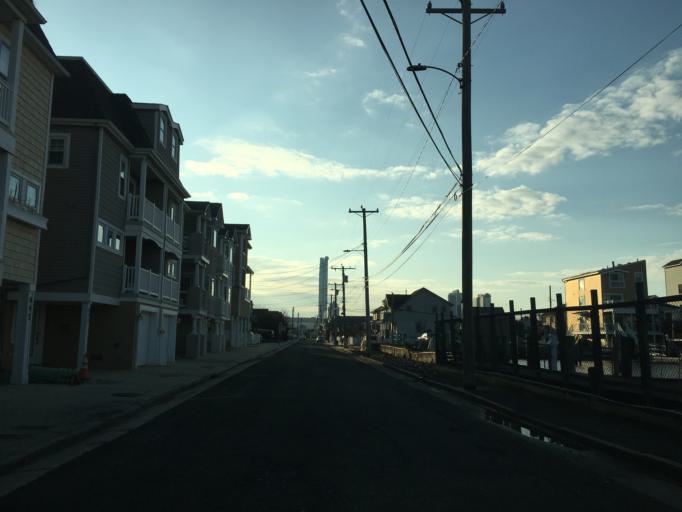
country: US
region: New Jersey
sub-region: Atlantic County
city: Atlantic City
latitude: 39.3758
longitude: -74.4234
